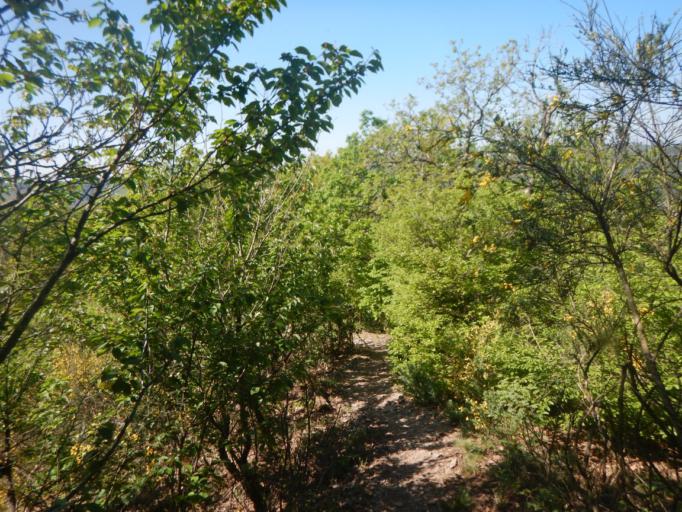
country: LU
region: Diekirch
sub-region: Canton de Diekirch
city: Bourscheid
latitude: 49.9101
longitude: 6.0928
